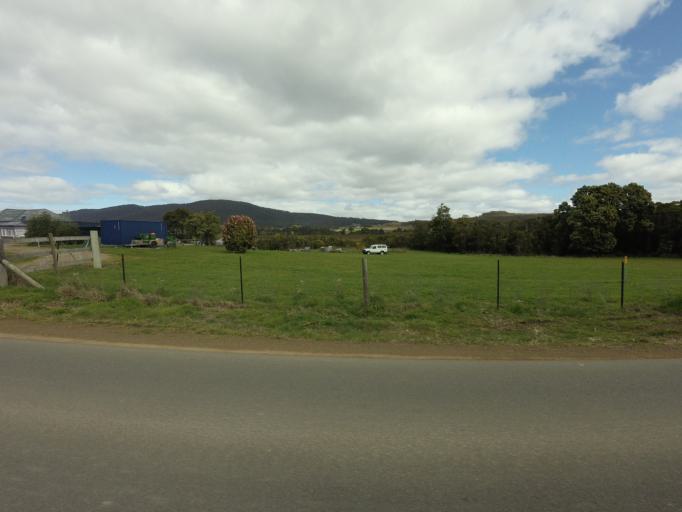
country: AU
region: Tasmania
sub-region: Huon Valley
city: Geeveston
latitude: -43.3240
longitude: 146.9792
